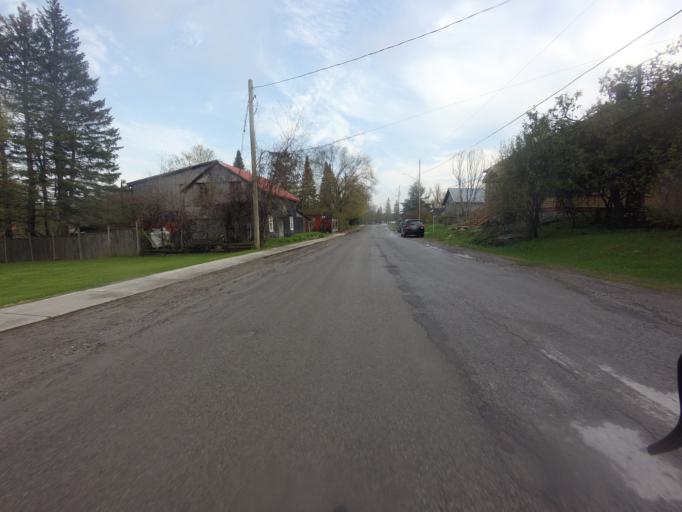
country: CA
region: Ontario
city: Carleton Place
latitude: 45.1929
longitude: -76.3261
